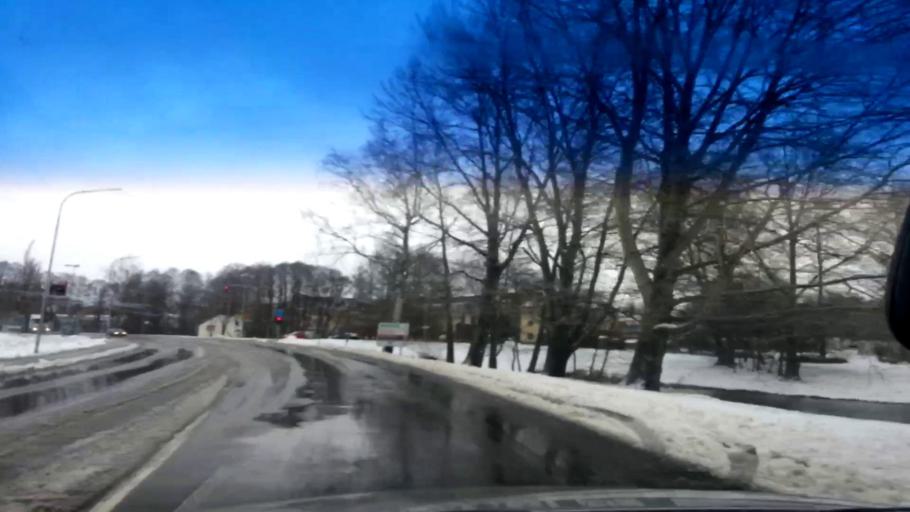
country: DE
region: Bavaria
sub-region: Upper Franconia
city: Selb
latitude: 50.1785
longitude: 12.1323
